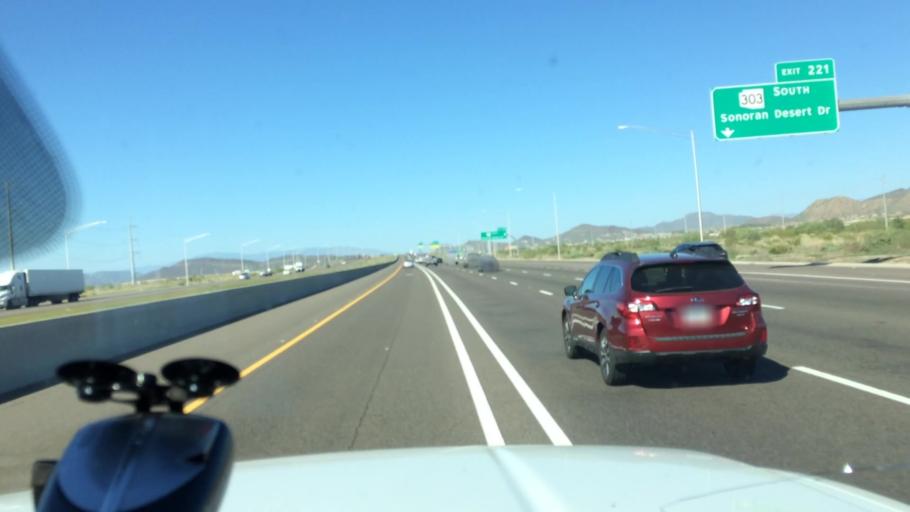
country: US
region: Arizona
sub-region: Maricopa County
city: Anthem
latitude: 33.7617
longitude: -112.1272
